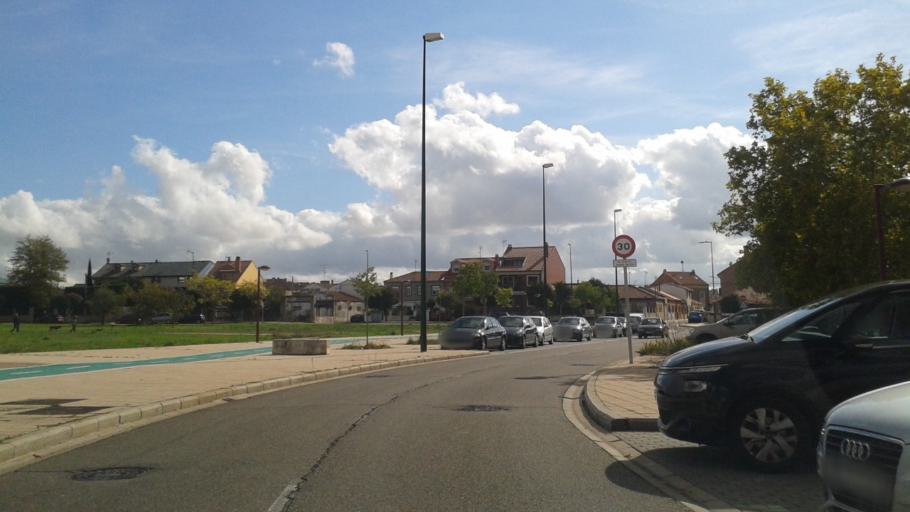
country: ES
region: Castille and Leon
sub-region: Provincia de Valladolid
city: Valladolid
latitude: 41.6605
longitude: -4.7067
